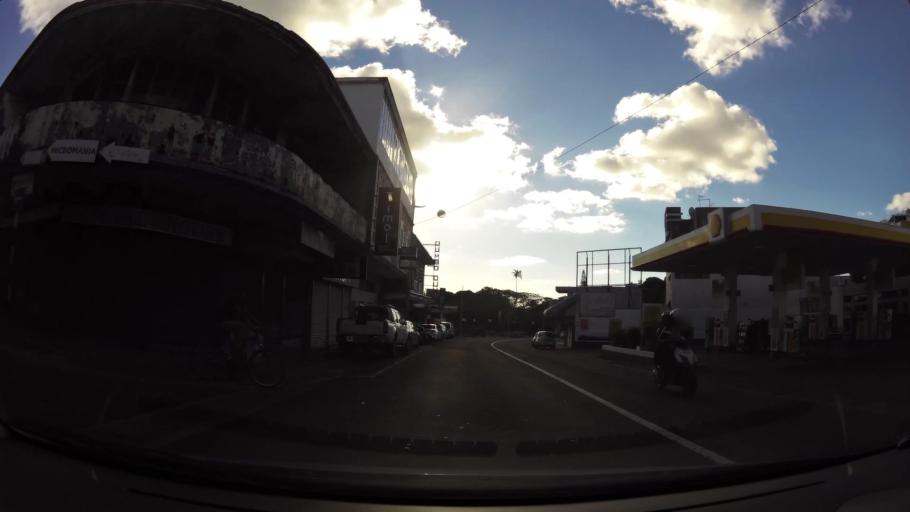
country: MU
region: Plaines Wilhems
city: Ebene
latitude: -20.2417
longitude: 57.4734
